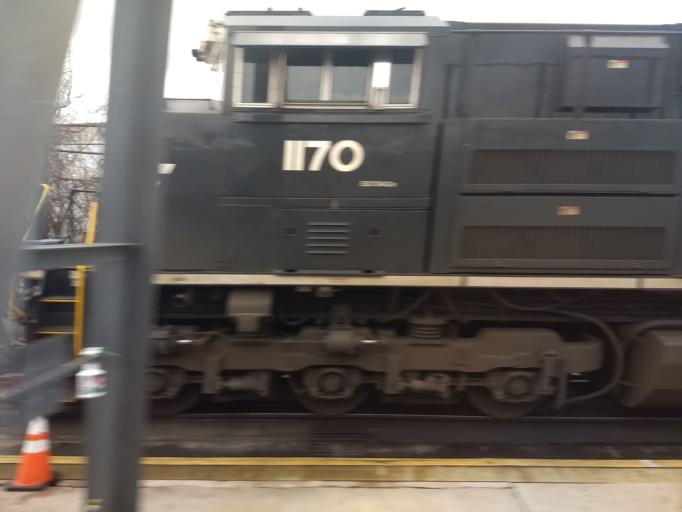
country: US
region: Pennsylvania
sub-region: Dauphin County
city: Harrisburg
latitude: 40.3021
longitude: -76.8938
